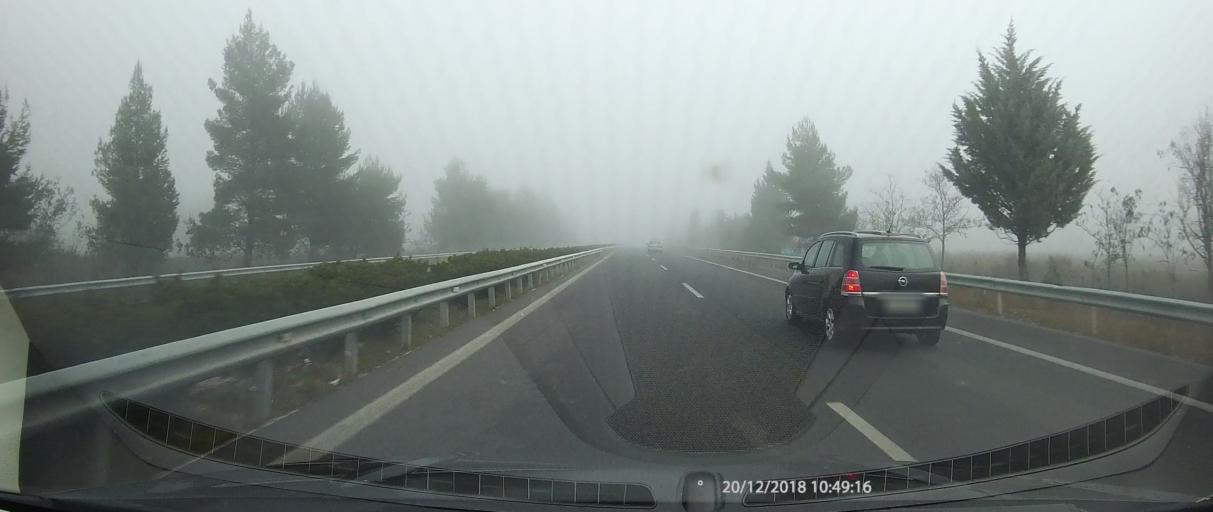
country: GR
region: Peloponnese
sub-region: Nomos Arkadias
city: Tripoli
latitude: 37.5355
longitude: 22.4134
